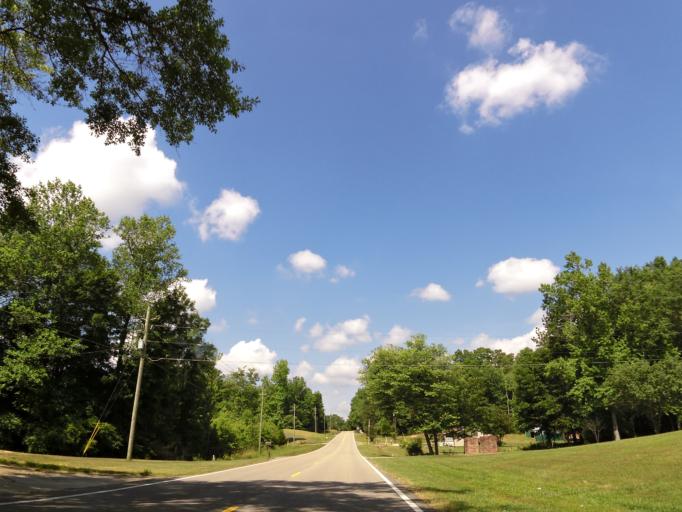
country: US
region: Alabama
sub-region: Marion County
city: Guin
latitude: 34.0098
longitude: -87.8478
